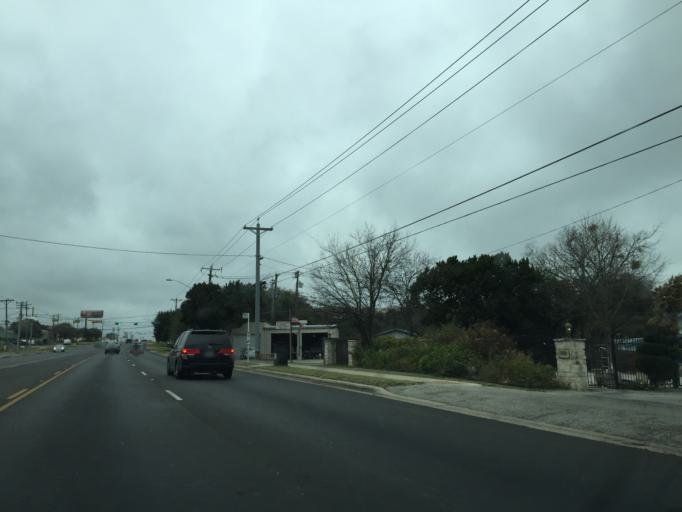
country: US
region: Texas
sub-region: Travis County
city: Wells Branch
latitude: 30.3856
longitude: -97.6845
